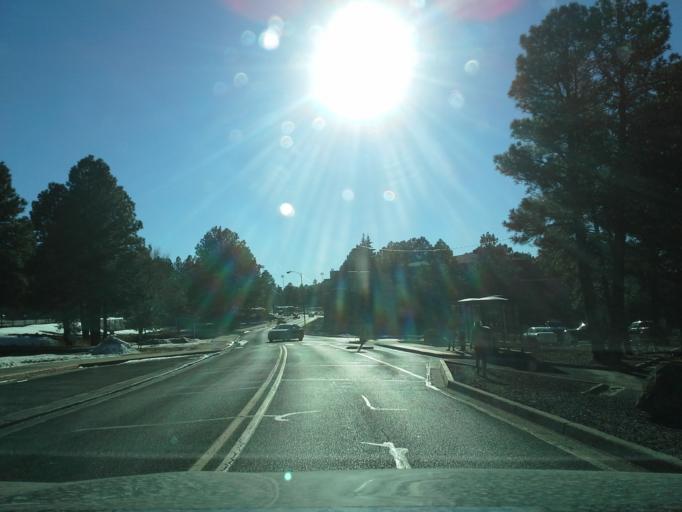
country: US
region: Arizona
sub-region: Coconino County
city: Flagstaff
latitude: 35.1773
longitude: -111.6540
